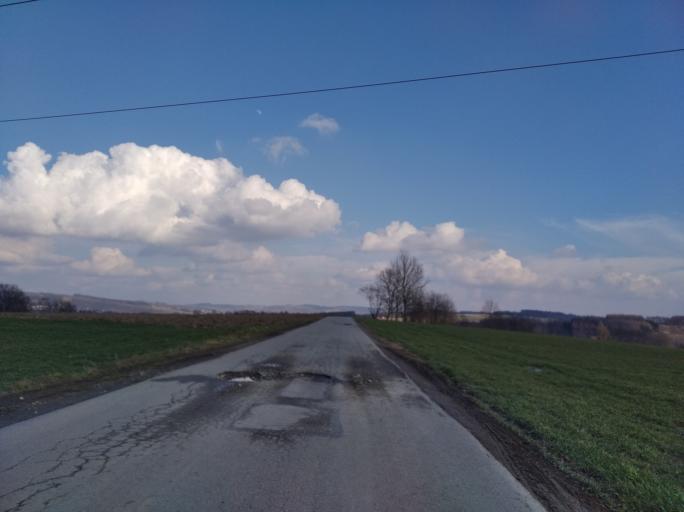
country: PL
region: Subcarpathian Voivodeship
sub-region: Powiat strzyzowski
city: Wysoka Strzyzowska
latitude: 49.8636
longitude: 21.7334
